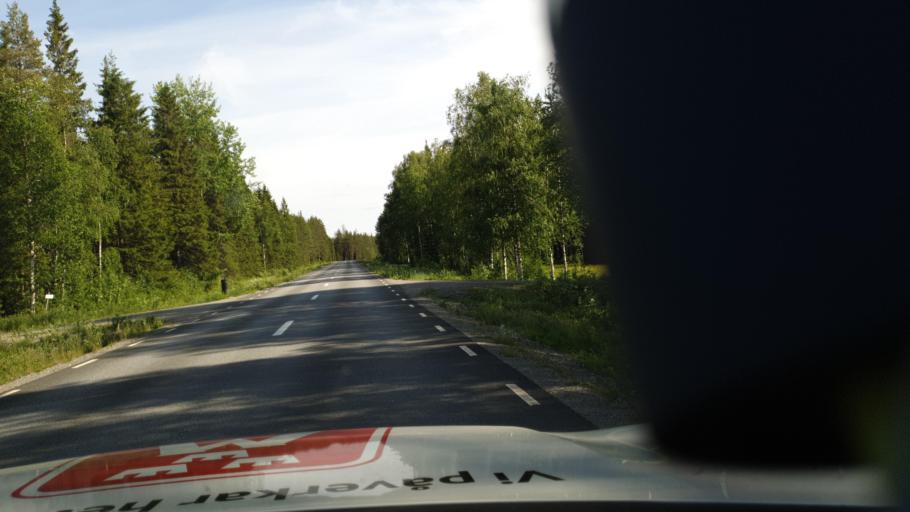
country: SE
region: Vaesterbotten
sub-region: Skelleftea Kommun
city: Forsbacka
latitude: 64.7210
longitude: 20.4161
